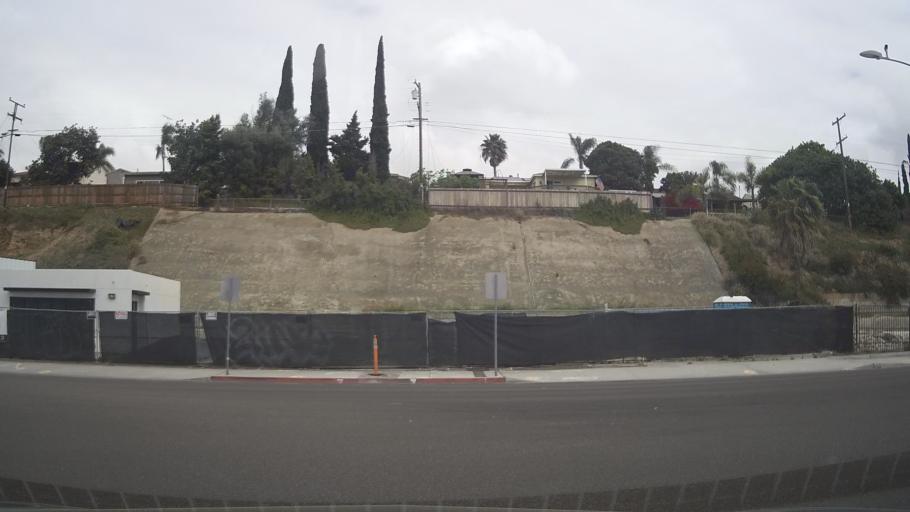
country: US
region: California
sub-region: San Diego County
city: Lemon Grove
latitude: 32.7550
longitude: -117.0431
